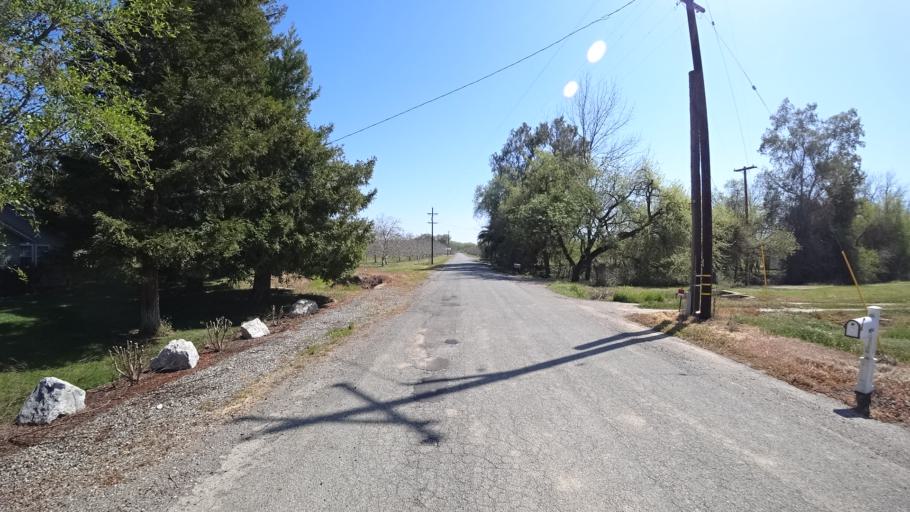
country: US
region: California
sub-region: Glenn County
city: Willows
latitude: 39.4356
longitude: -122.0183
